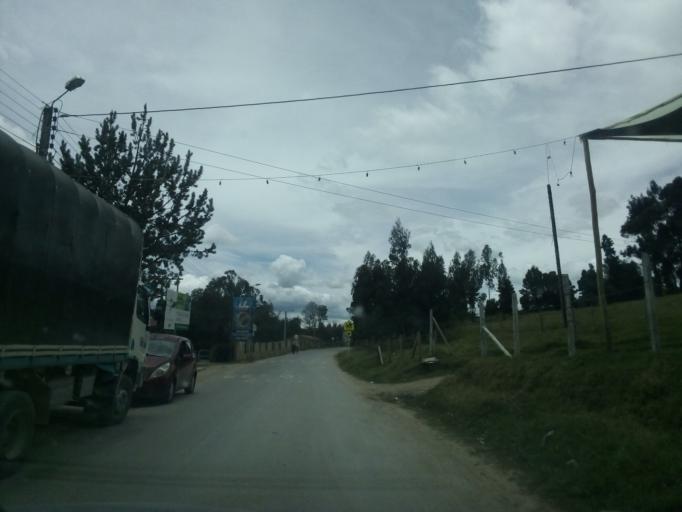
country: CO
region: Boyaca
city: Toca
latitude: 5.5713
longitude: -73.1820
